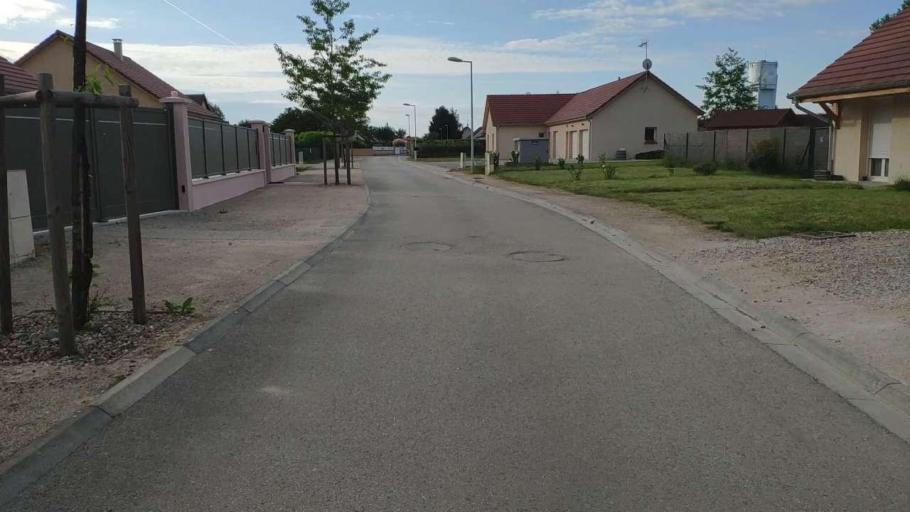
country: FR
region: Franche-Comte
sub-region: Departement du Jura
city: Bletterans
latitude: 46.7514
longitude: 5.4439
